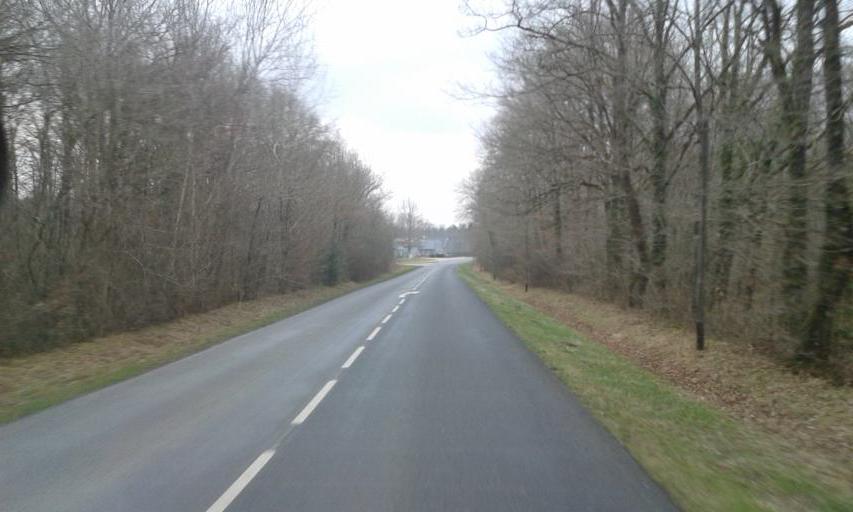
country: FR
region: Centre
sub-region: Departement du Loir-et-Cher
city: Dhuizon
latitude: 47.6461
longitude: 1.6675
